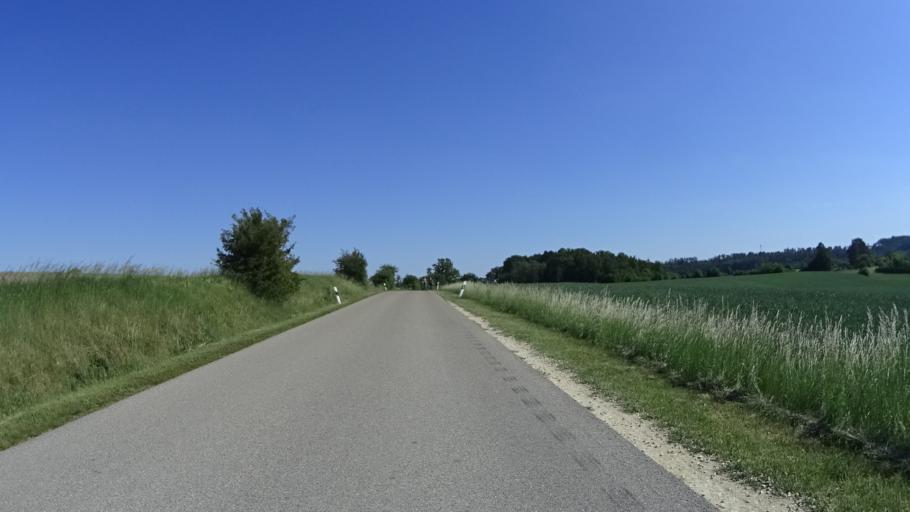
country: DE
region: Bavaria
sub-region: Regierungsbezirk Mittelfranken
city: Dombuhl
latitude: 49.2239
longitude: 10.3001
